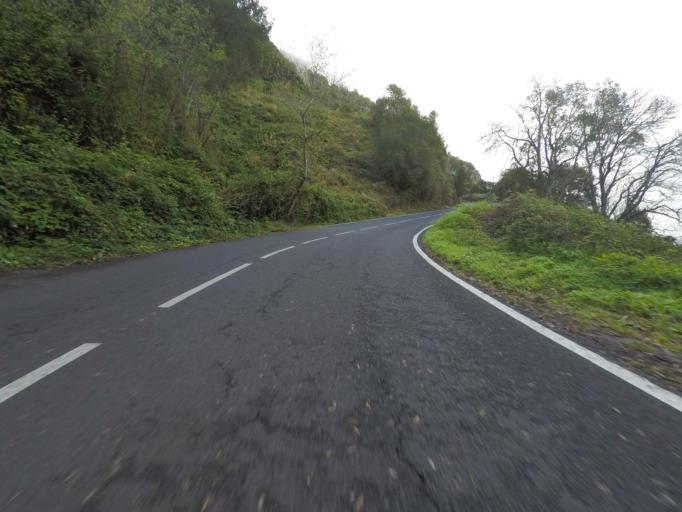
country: ES
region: Canary Islands
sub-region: Provincia de Santa Cruz de Tenerife
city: Hermigua
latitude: 28.1295
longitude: -17.2109
